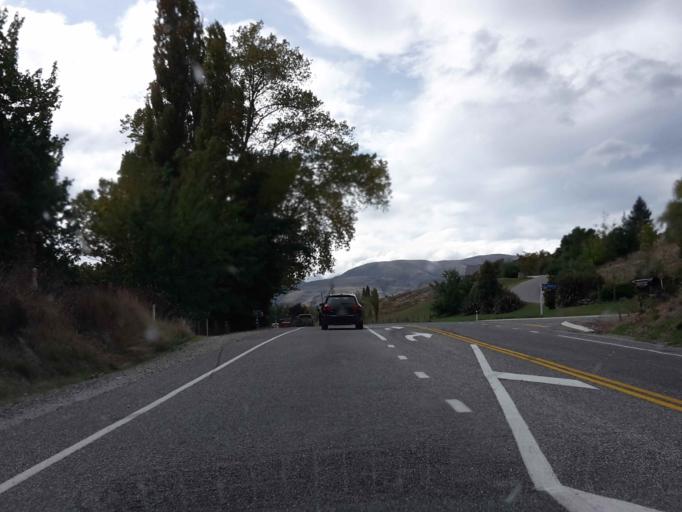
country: NZ
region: Otago
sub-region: Queenstown-Lakes District
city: Arrowtown
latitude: -44.9940
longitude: 168.8056
